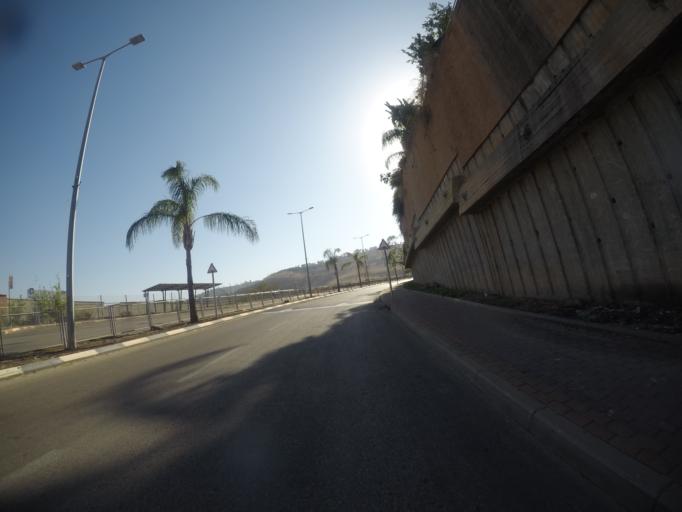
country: IL
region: Northern District
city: Tiberias
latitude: 32.7833
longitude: 35.5310
